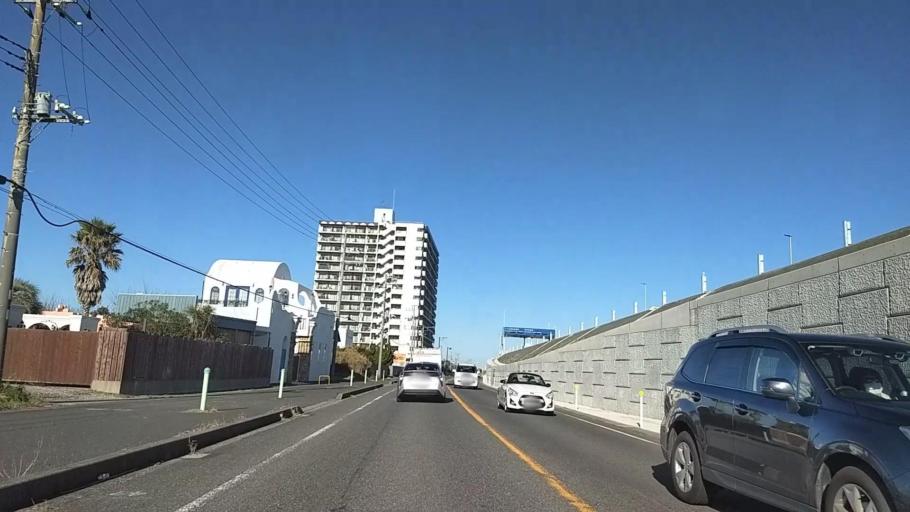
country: JP
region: Chiba
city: Togane
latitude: 35.4514
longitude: 140.4032
